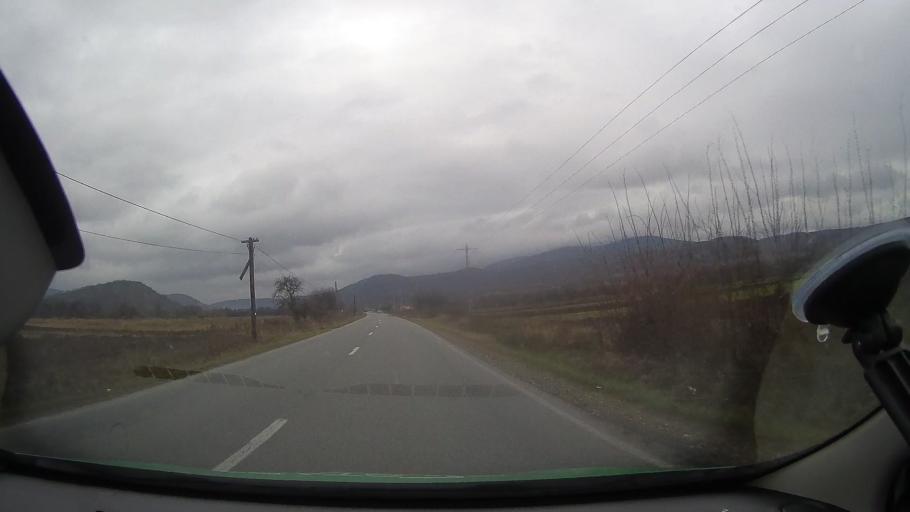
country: RO
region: Arad
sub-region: Comuna Buteni
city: Buteni
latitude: 46.3173
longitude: 22.1350
